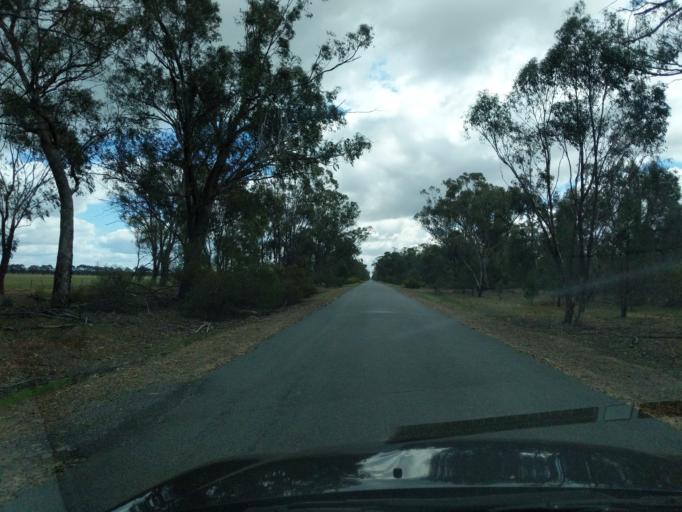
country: AU
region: New South Wales
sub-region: Coolamon
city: Coolamon
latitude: -34.9375
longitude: 146.9690
